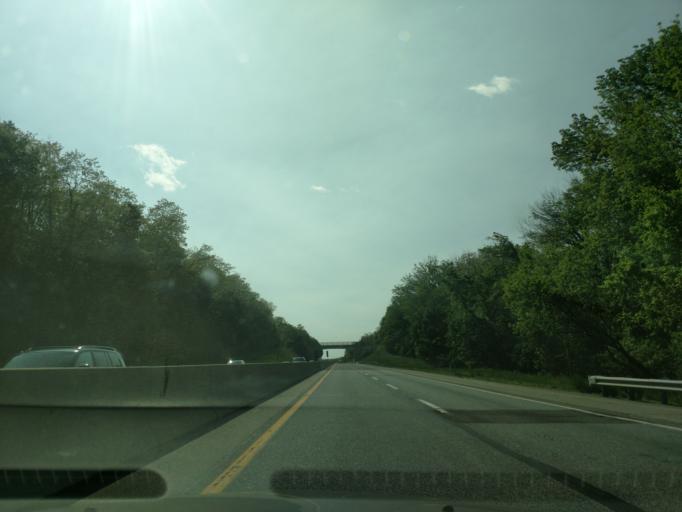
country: US
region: Pennsylvania
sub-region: Lancaster County
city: Denver
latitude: 40.2423
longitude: -76.1476
